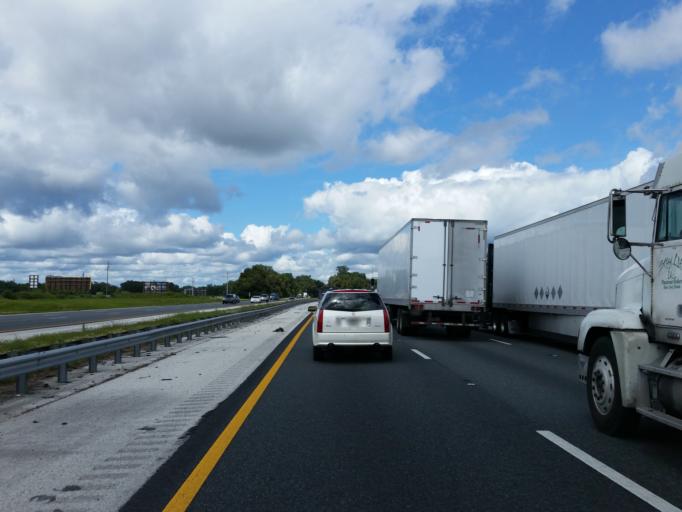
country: US
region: Florida
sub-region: Sumter County
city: Wildwood
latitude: 28.9071
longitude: -82.1077
